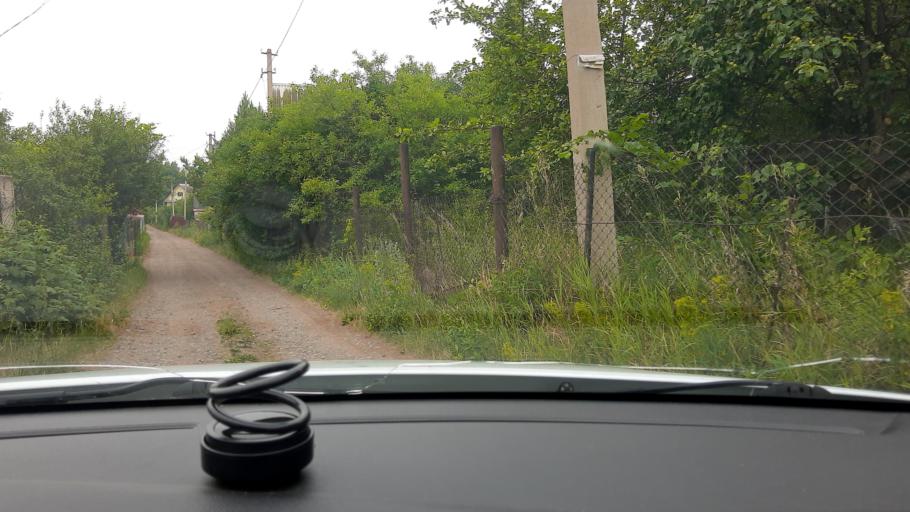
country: RU
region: Bashkortostan
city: Avdon
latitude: 54.6389
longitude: 55.5739
